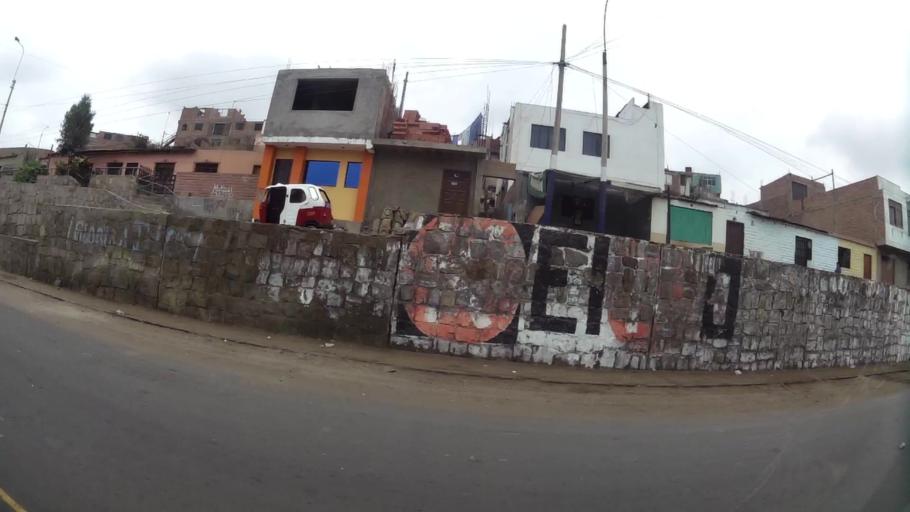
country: PE
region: Lima
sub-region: Lima
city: Surco
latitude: -12.1948
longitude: -77.0004
